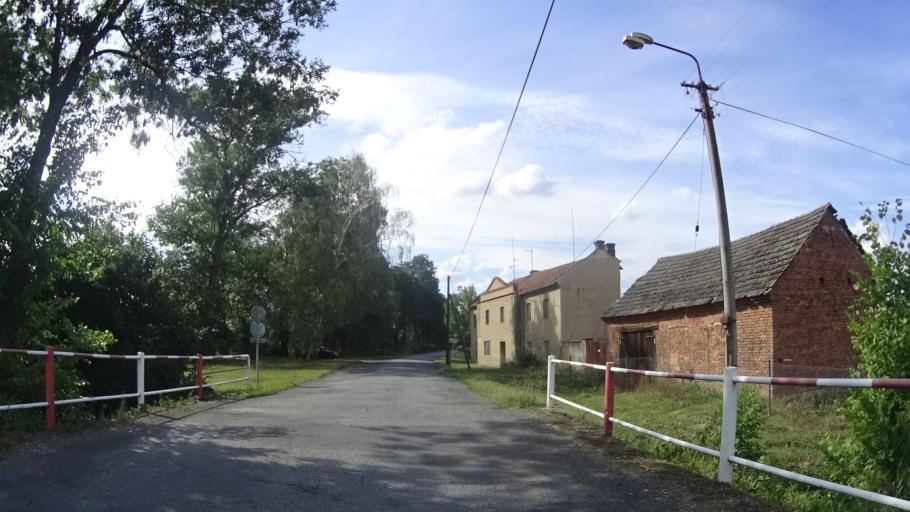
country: CZ
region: Olomoucky
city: Moravicany
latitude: 49.7489
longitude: 16.9730
